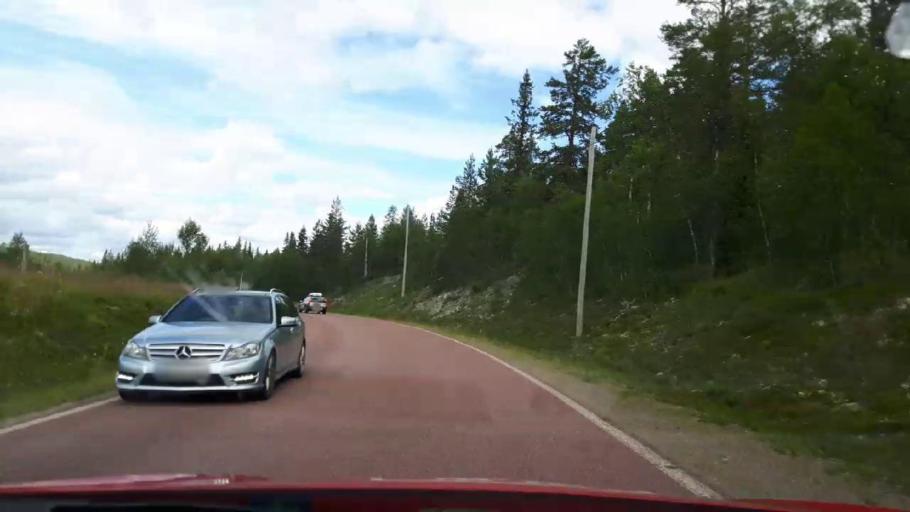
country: NO
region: Hedmark
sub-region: Trysil
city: Innbygda
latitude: 61.9955
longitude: 12.9820
